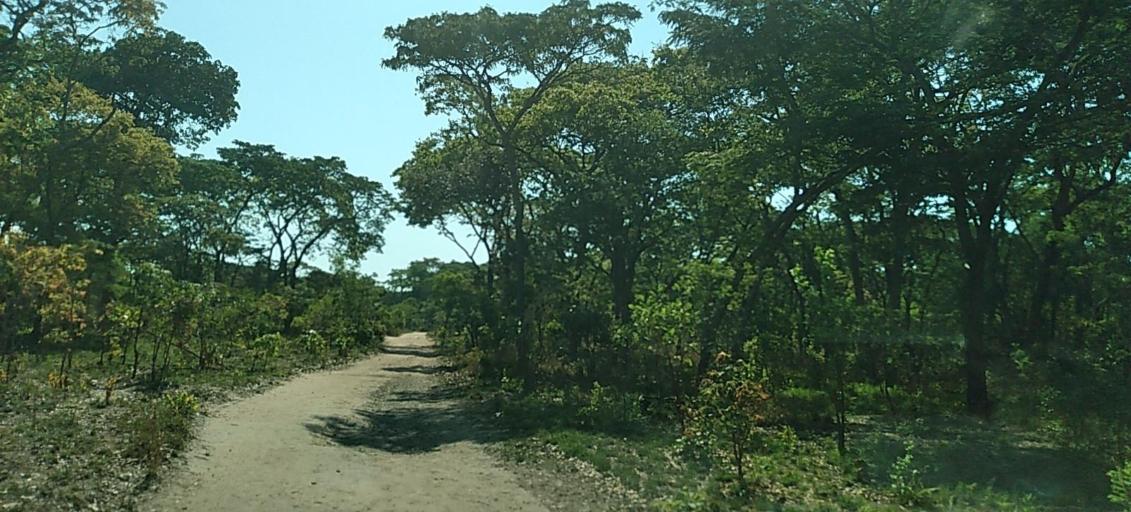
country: ZM
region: Central
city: Mkushi
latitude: -13.4702
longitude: 28.9718
